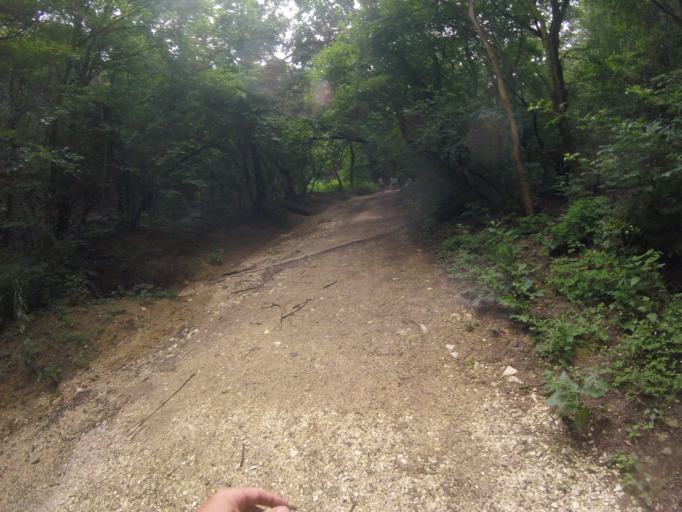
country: HU
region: Pest
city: Toeroekbalint
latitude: 47.4245
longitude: 18.9127
